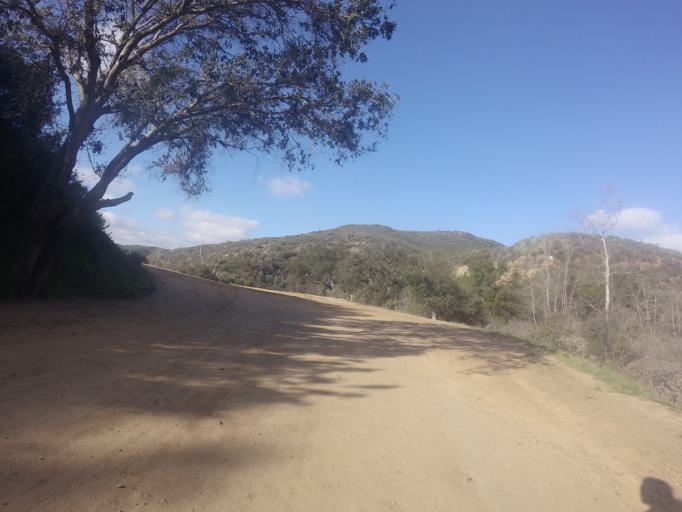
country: US
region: California
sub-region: Orange County
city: Foothill Ranch
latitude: 33.7771
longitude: -117.6758
